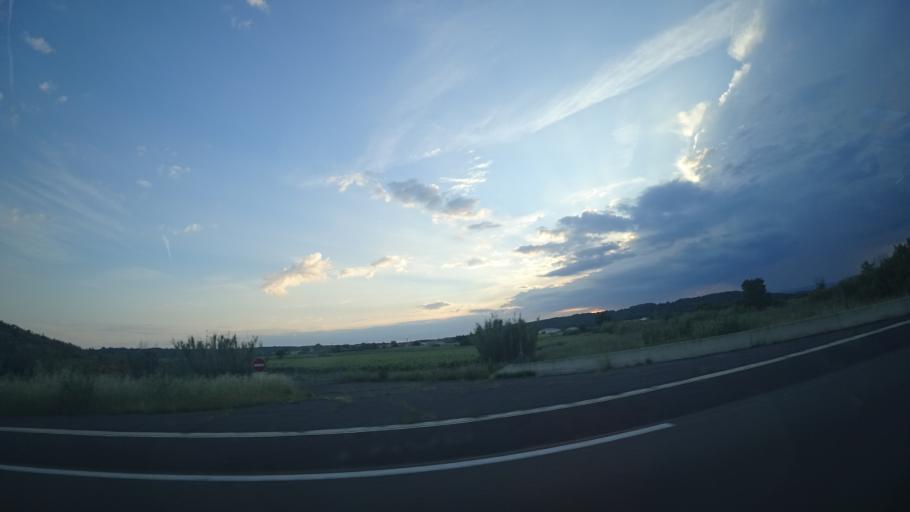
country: FR
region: Languedoc-Roussillon
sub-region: Departement de l'Herault
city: Lezignan-la-Cebe
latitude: 43.5004
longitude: 3.4451
